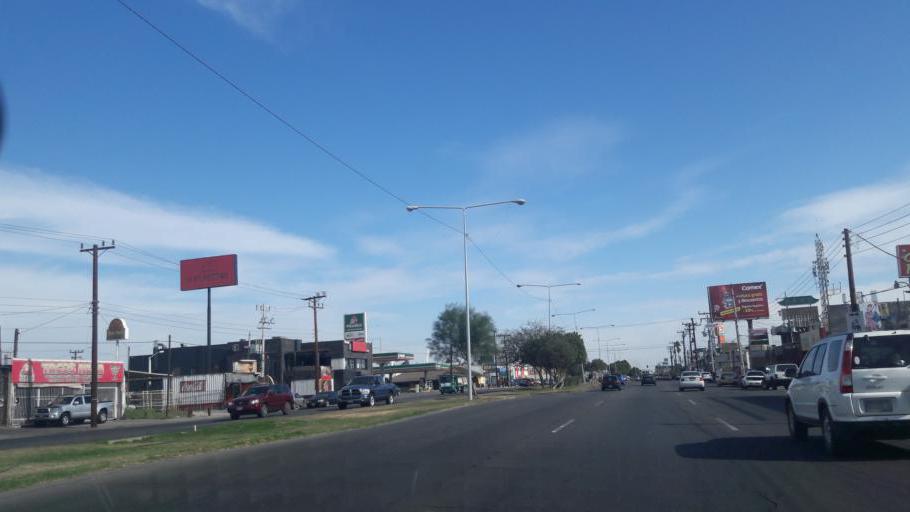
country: MX
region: Baja California
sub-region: Mexicali
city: Mexicali
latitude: 32.6237
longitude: -115.4836
